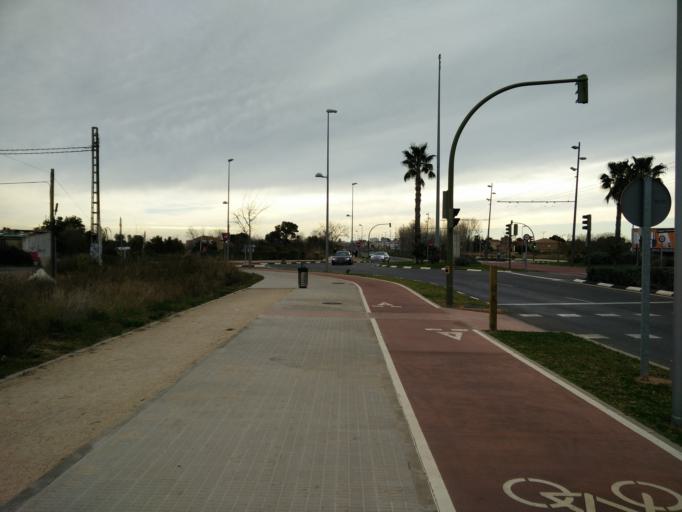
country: ES
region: Valencia
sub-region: Provincia de Castello
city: Castello de la Plana
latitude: 39.9800
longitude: -0.0051
